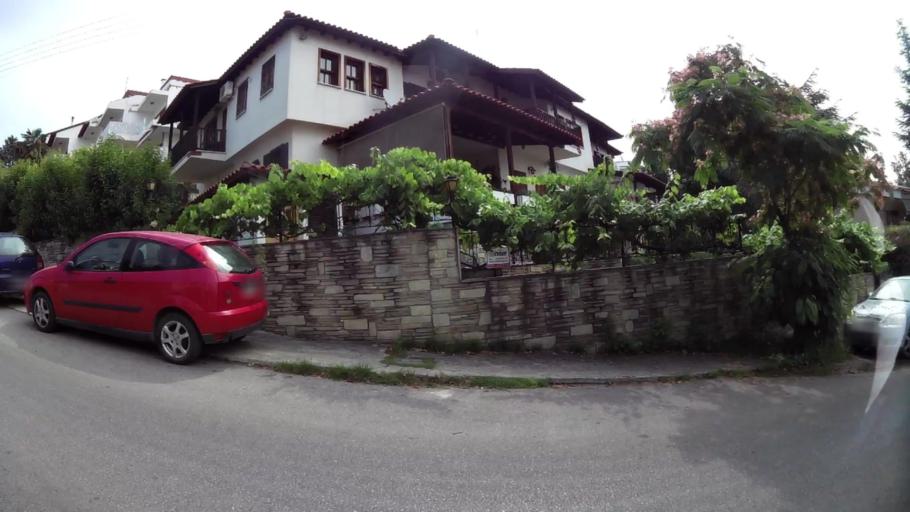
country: GR
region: Central Macedonia
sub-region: Nomos Thessalonikis
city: Panorama
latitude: 40.5787
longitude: 23.0215
